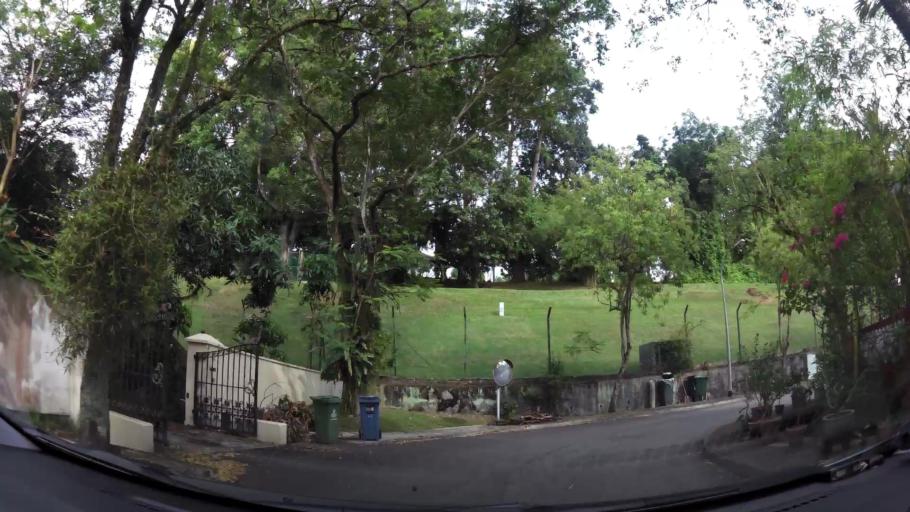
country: SG
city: Singapore
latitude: 1.3255
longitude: 103.8183
